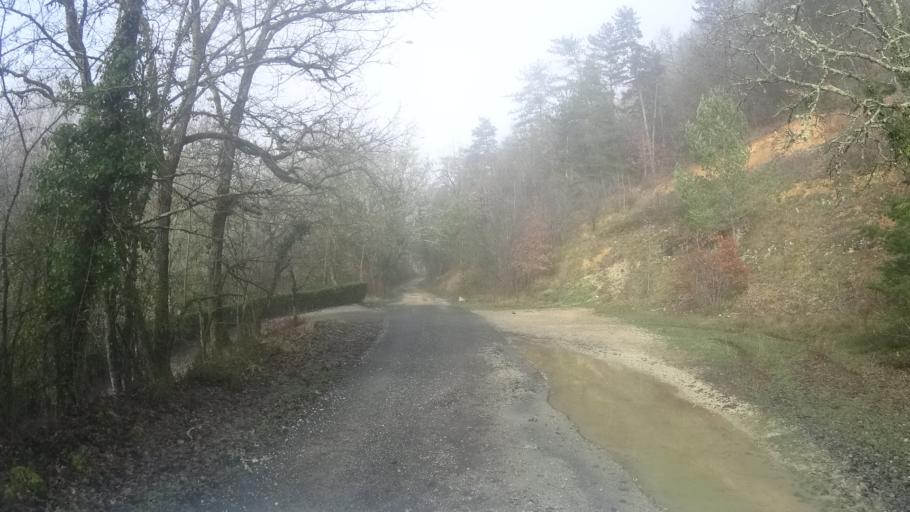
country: FR
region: Aquitaine
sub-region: Departement de la Dordogne
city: Terrasson-Lavilledieu
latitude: 45.0907
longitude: 1.2669
